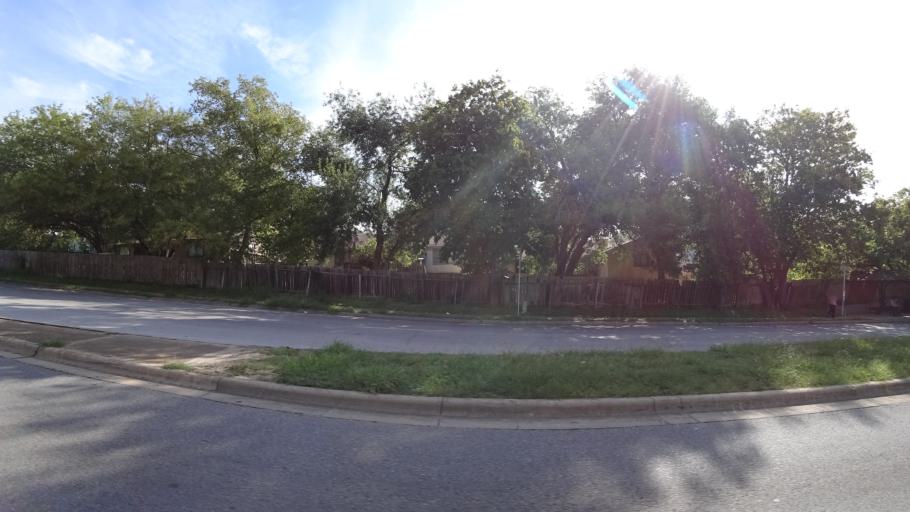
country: US
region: Texas
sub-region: Travis County
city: Onion Creek
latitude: 30.1925
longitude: -97.7447
